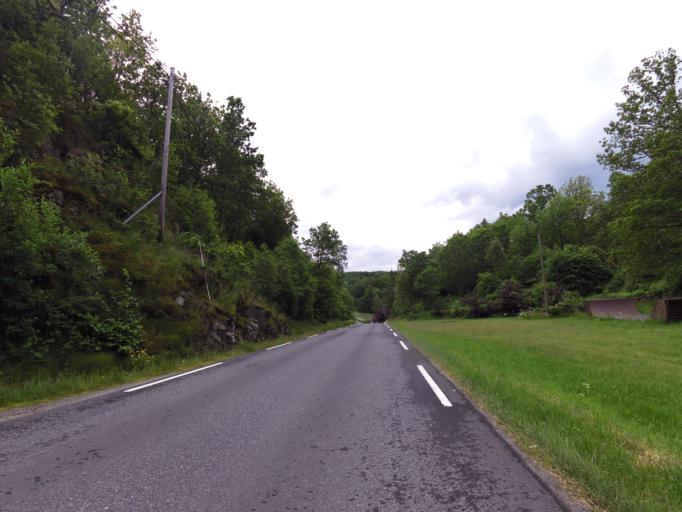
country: NO
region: Vest-Agder
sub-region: Lyngdal
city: Lyngdal
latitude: 58.1032
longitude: 6.9619
